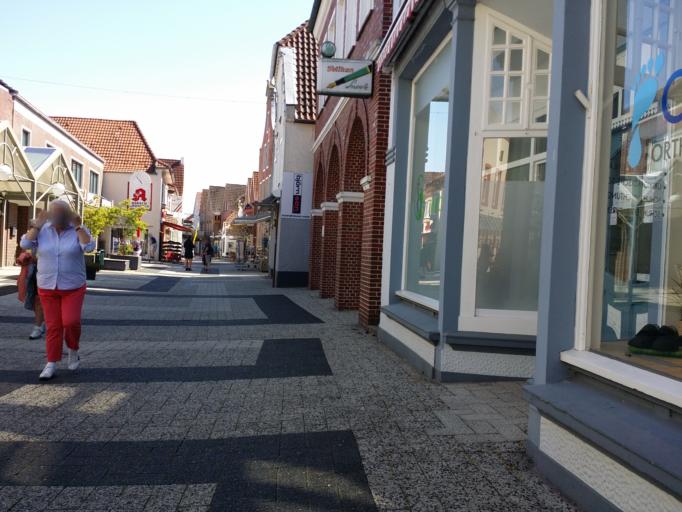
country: DE
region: Lower Saxony
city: Esens
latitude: 53.6462
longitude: 7.6128
